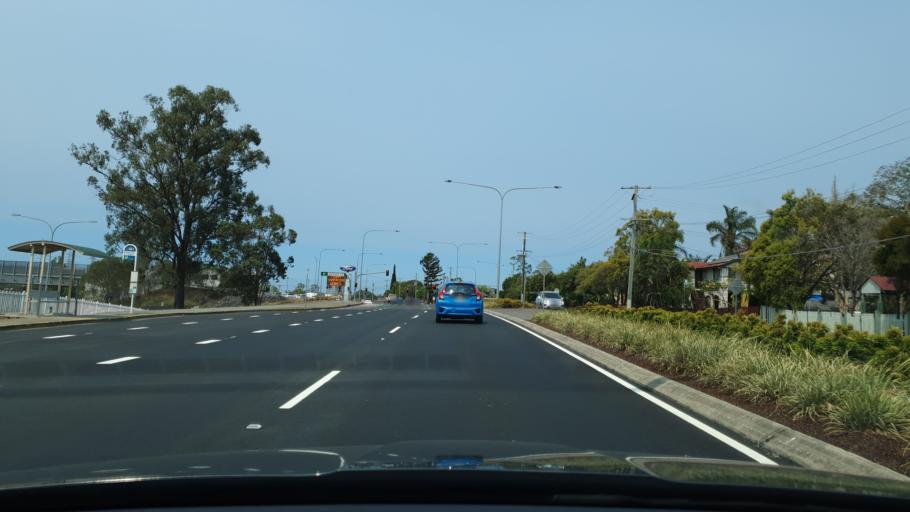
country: AU
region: Queensland
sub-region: Ipswich
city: Bundamba
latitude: -27.6036
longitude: 152.8226
